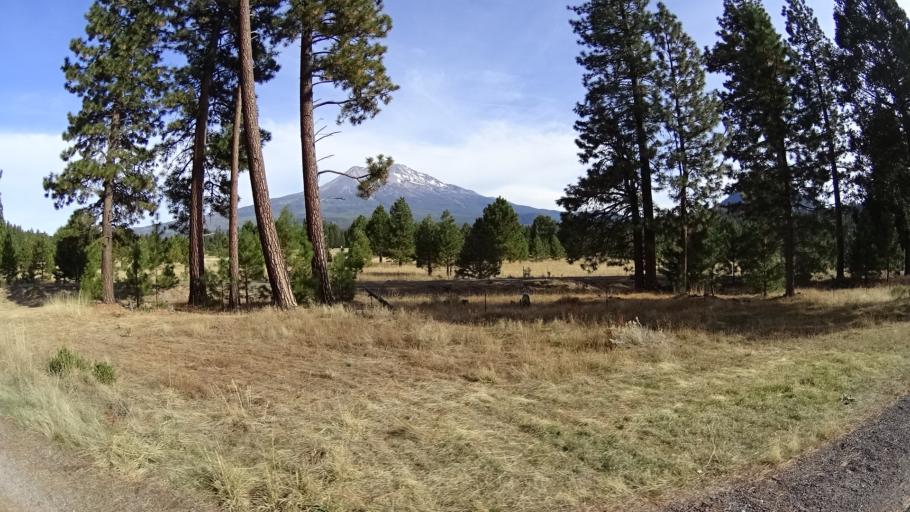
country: US
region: California
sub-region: Siskiyou County
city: Weed
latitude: 41.3984
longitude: -122.3894
